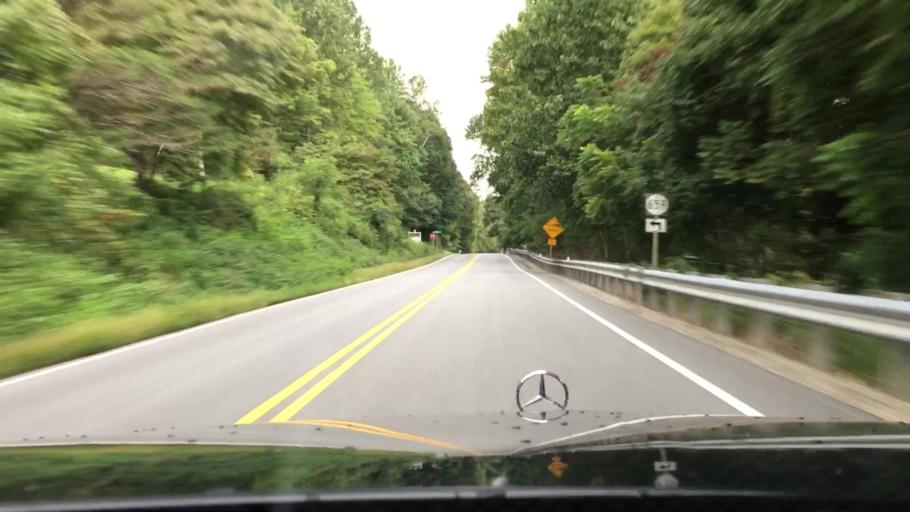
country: US
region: Virginia
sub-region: Nelson County
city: Lovingston
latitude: 37.8030
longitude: -78.9536
